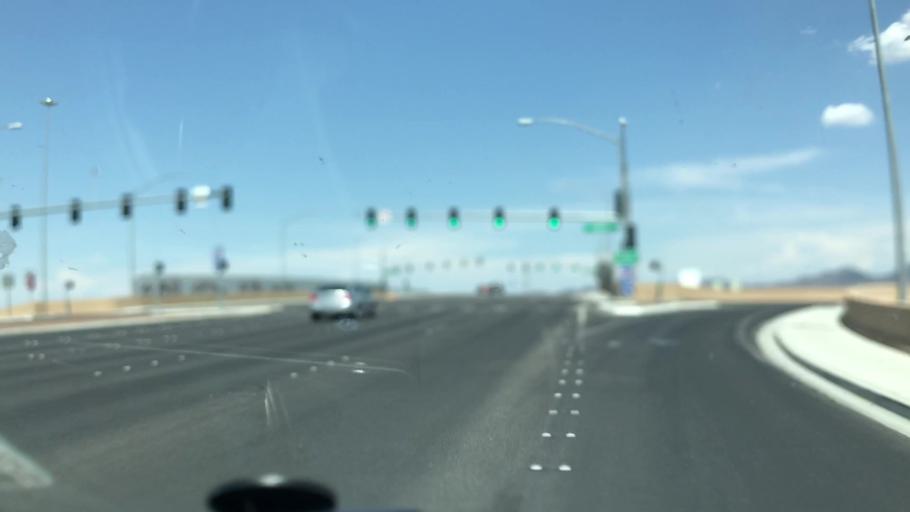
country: US
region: Nevada
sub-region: Clark County
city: Enterprise
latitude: 35.9989
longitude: -115.1821
